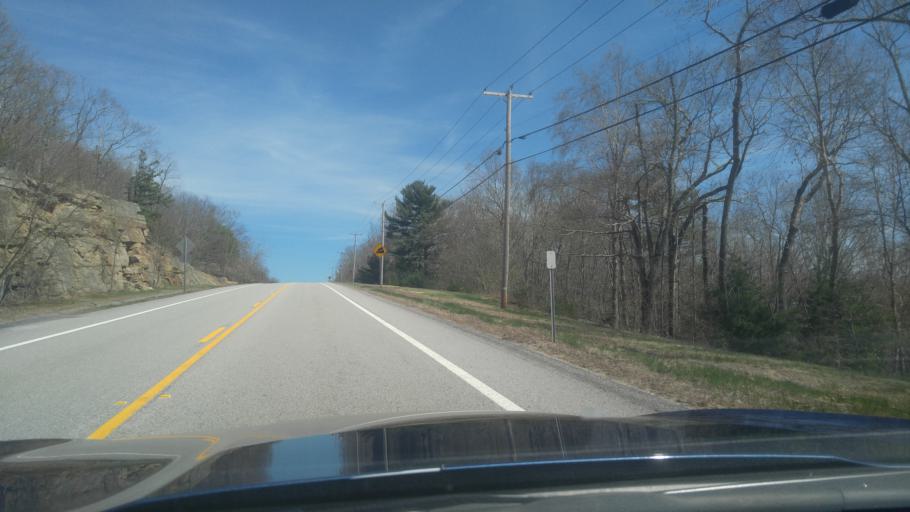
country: US
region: Rhode Island
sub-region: Washington County
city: Hope Valley
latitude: 41.5749
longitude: -71.7392
